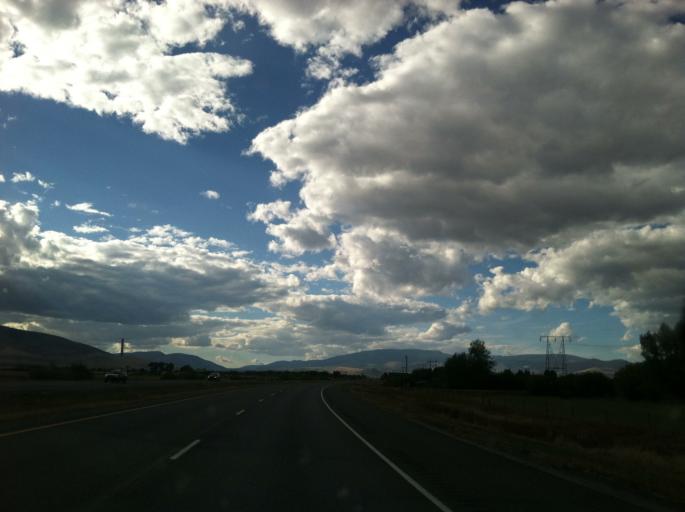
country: US
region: Montana
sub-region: Deer Lodge County
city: Warm Springs
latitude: 46.0973
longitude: -112.8276
